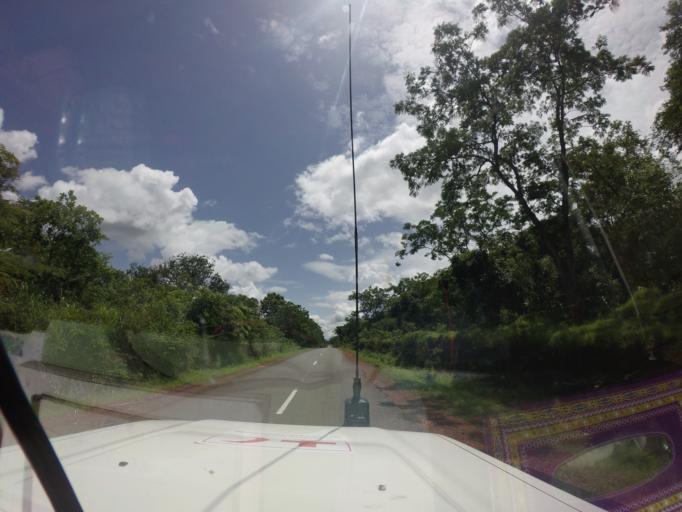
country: SL
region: Northern Province
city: Bindi
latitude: 10.1610
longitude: -11.2748
